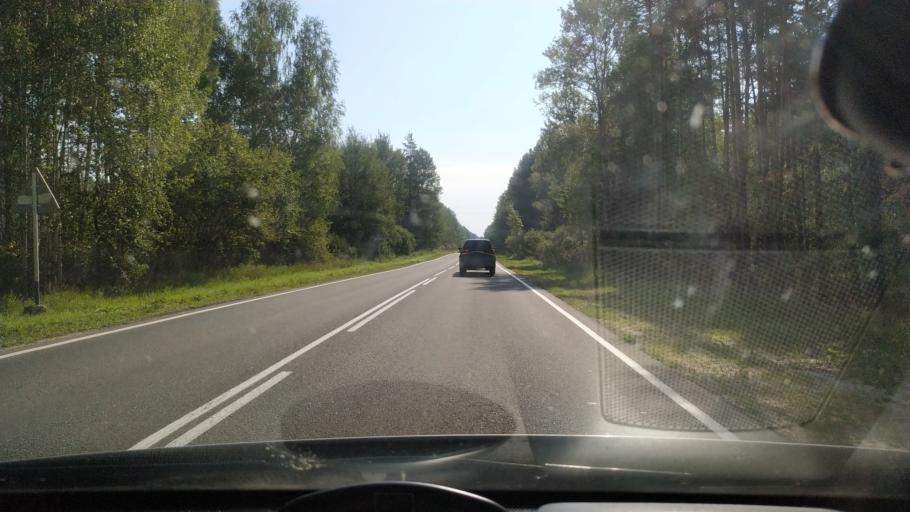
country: RU
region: Rjazan
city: Spas-Klepiki
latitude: 55.2234
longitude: 40.0739
